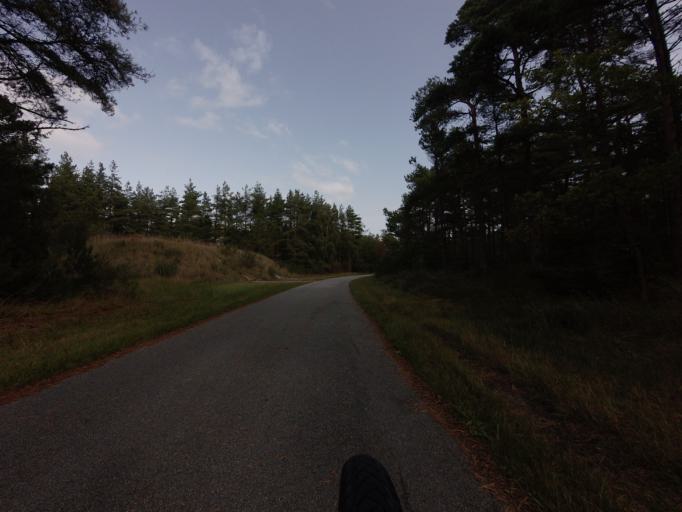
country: DK
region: North Denmark
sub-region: Frederikshavn Kommune
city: Strandby
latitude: 57.6405
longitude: 10.4322
